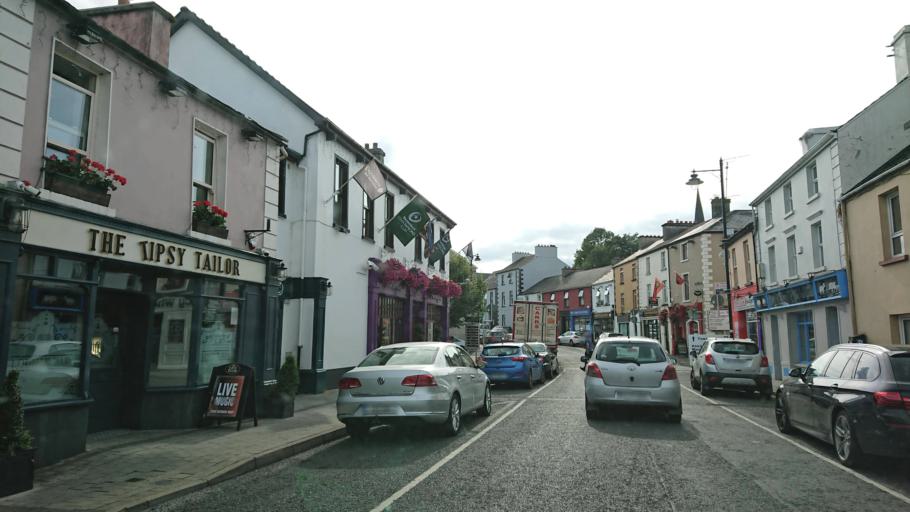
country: IE
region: Connaught
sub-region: County Leitrim
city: Carrick-on-Shannon
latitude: 53.9469
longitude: -8.0920
